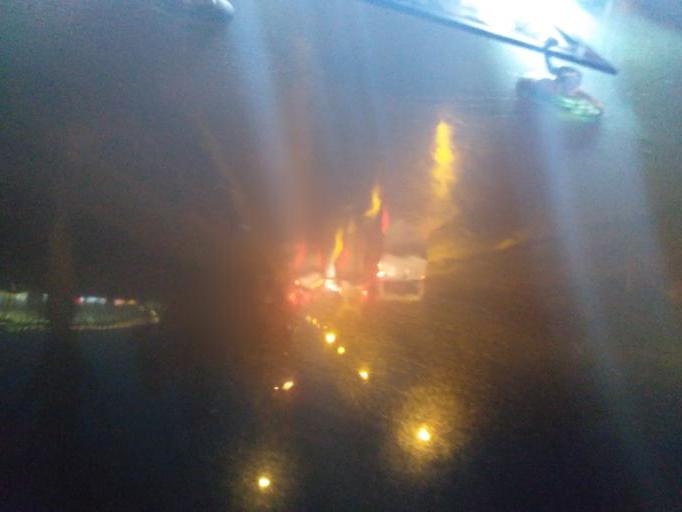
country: TR
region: Ankara
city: Ankara
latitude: 39.9660
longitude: 32.8201
